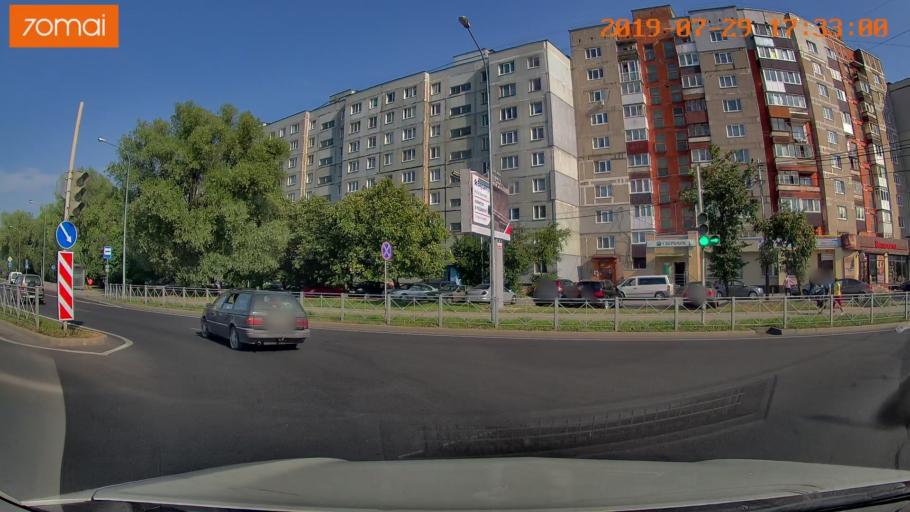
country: RU
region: Kaliningrad
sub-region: Gorod Kaliningrad
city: Kaliningrad
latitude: 54.7404
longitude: 20.4954
